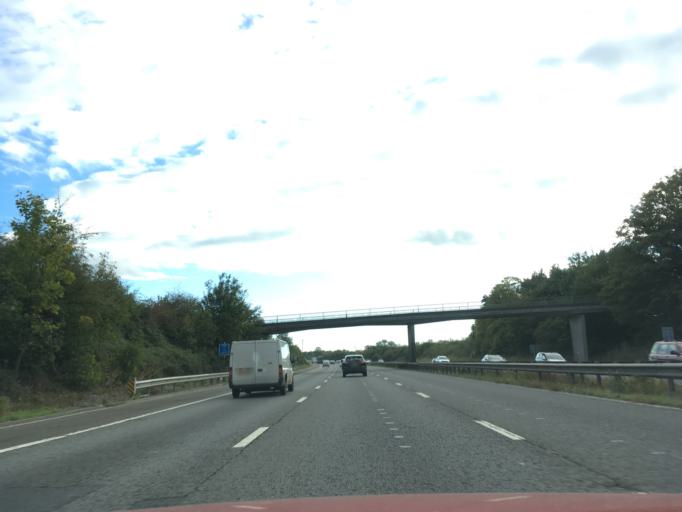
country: GB
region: England
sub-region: South Gloucestershire
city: Falfield
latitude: 51.6242
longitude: -2.4614
